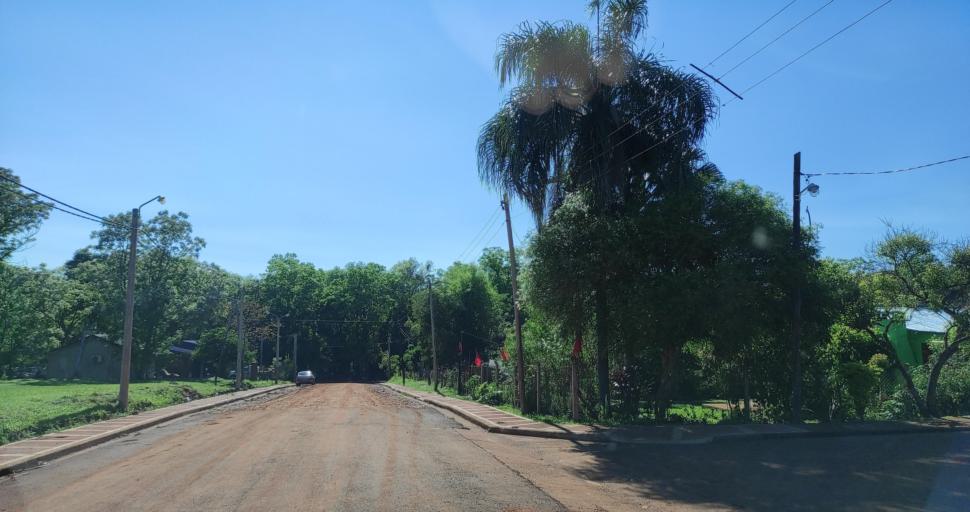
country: AR
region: Misiones
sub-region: Departamento de Candelaria
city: Loreto
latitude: -27.3309
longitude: -55.5247
